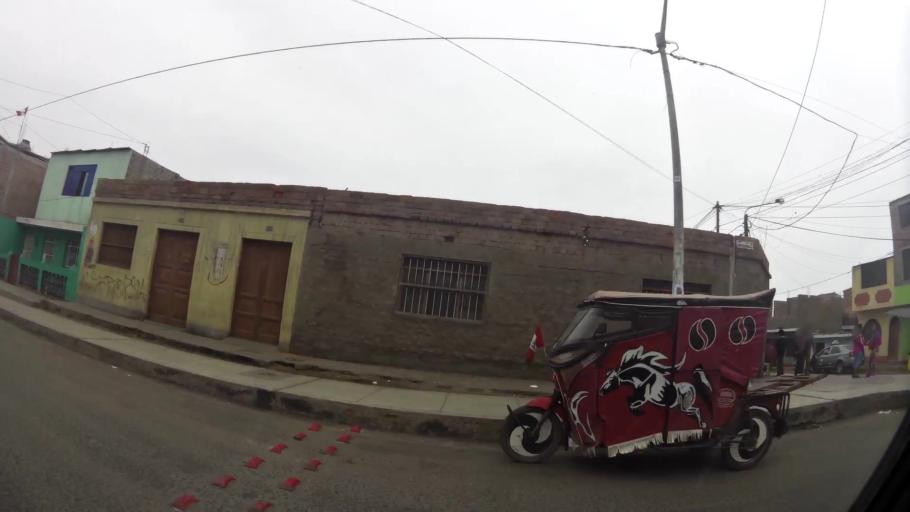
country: PE
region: Ancash
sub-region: Provincia de Santa
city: Chimbote
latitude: -9.0661
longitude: -78.5856
